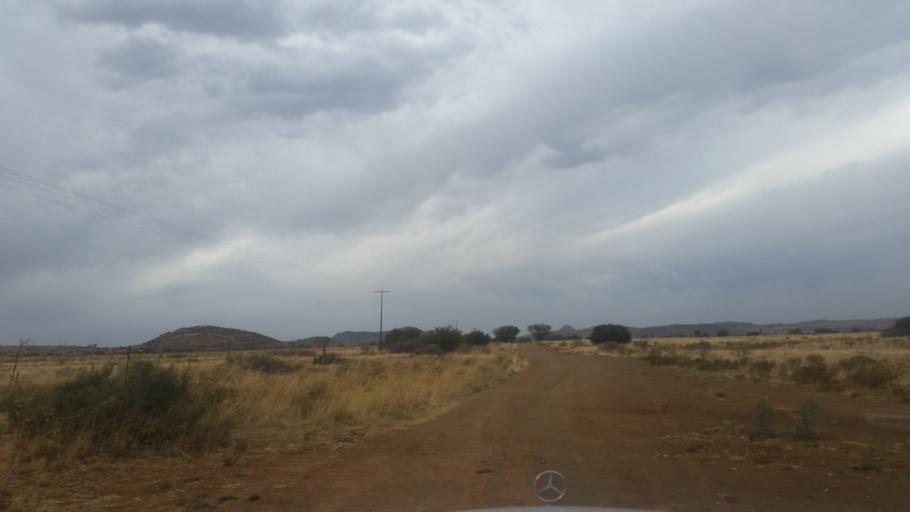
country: ZA
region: Orange Free State
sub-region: Xhariep District Municipality
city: Trompsburg
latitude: -30.5037
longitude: 25.9479
